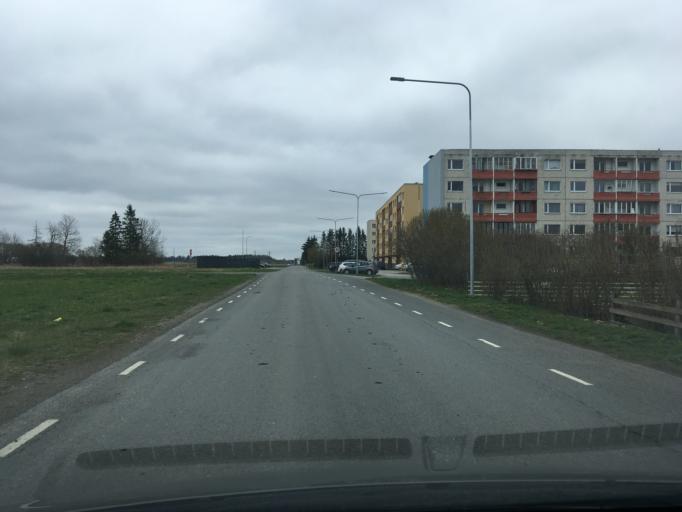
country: EE
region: Harju
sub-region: Rae vald
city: Vaida
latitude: 59.2890
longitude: 24.9794
